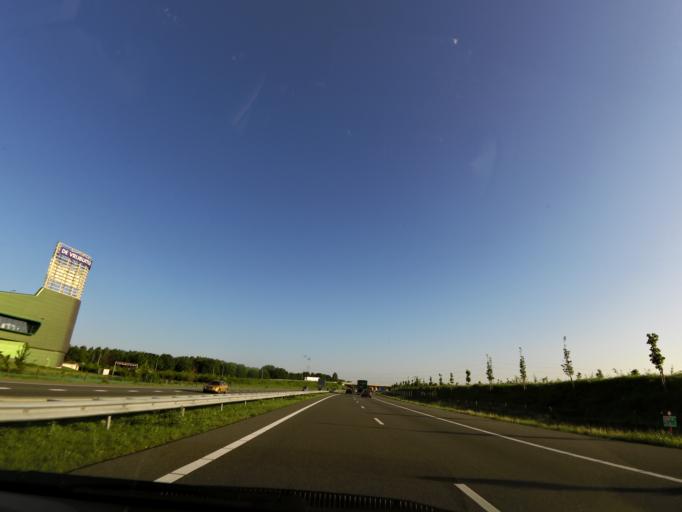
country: NL
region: Limburg
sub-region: Gemeente Roermond
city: Leeuwen
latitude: 51.2124
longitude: 6.0204
